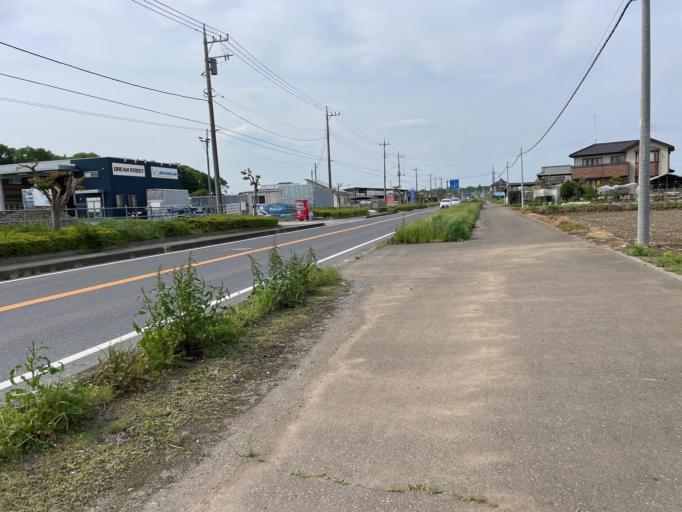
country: JP
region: Tochigi
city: Mibu
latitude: 36.3879
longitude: 139.8039
